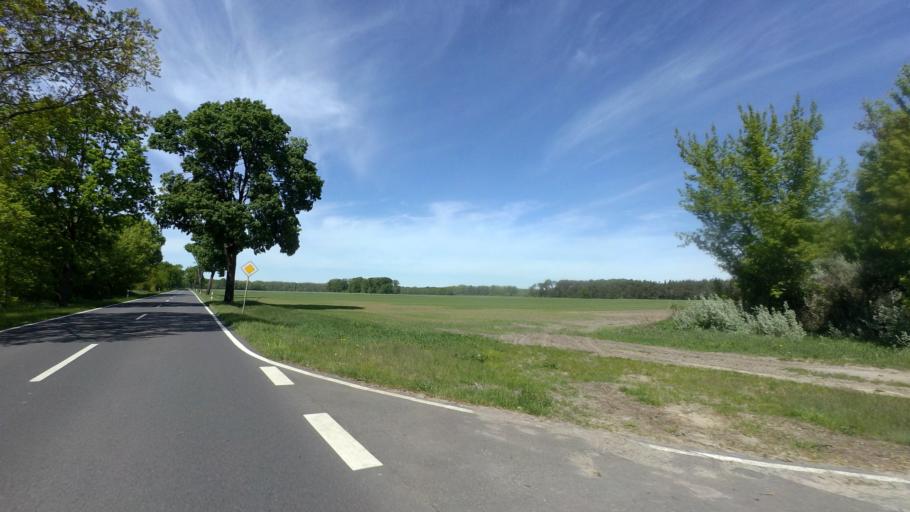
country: DE
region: Brandenburg
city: Baruth
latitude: 52.0734
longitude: 13.4613
